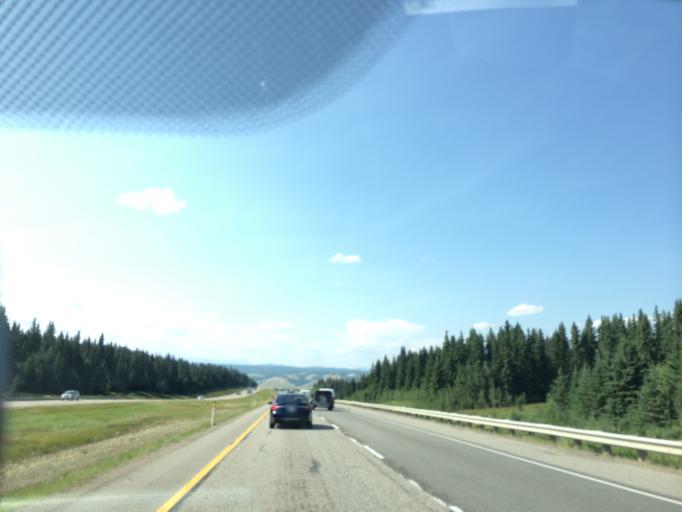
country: CA
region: Alberta
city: Cochrane
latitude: 51.1505
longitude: -114.7396
